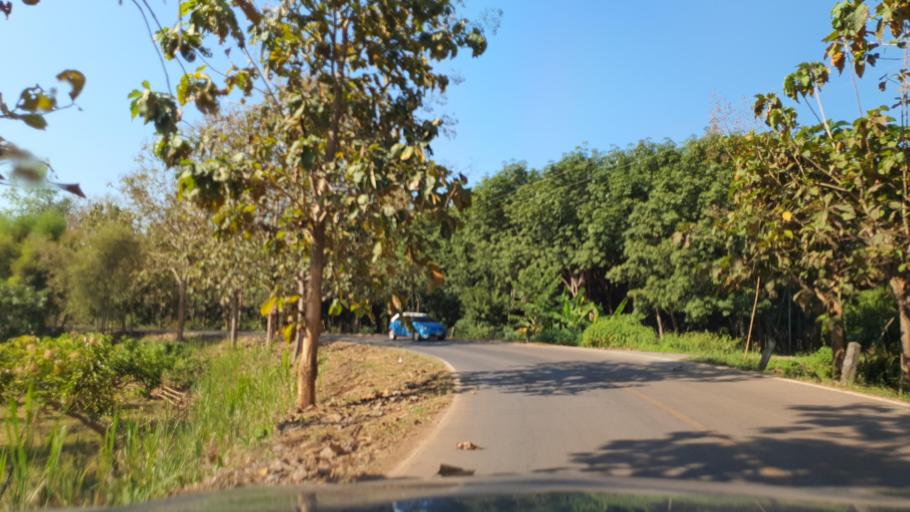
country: TH
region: Nan
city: Pua
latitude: 19.1226
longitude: 100.9165
